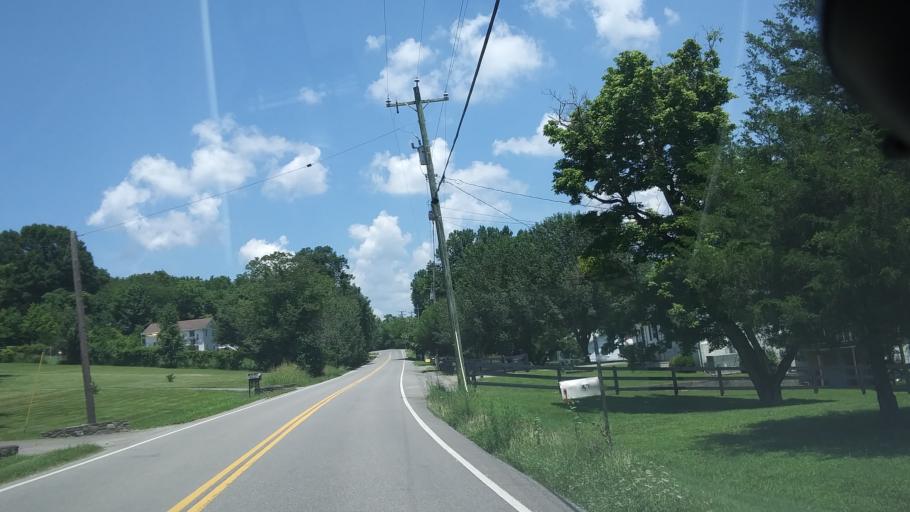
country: US
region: Tennessee
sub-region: Davidson County
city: Belle Meade
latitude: 36.1291
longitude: -86.9282
